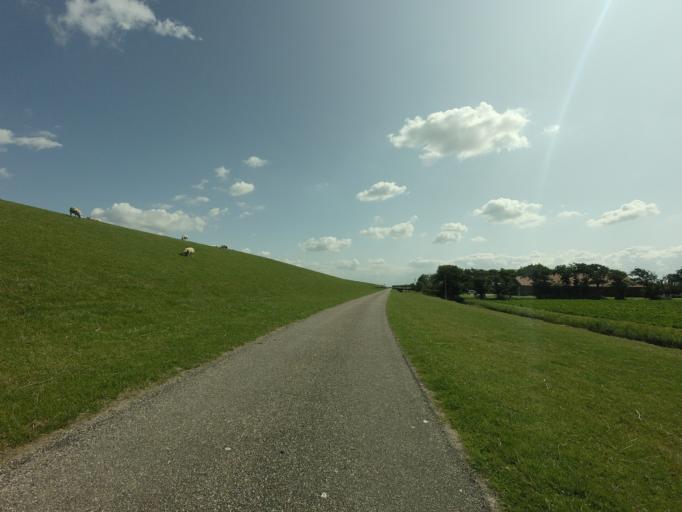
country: NL
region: Friesland
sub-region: Gemeente Ferwerderadiel
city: Hallum
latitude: 53.3235
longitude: 5.7385
